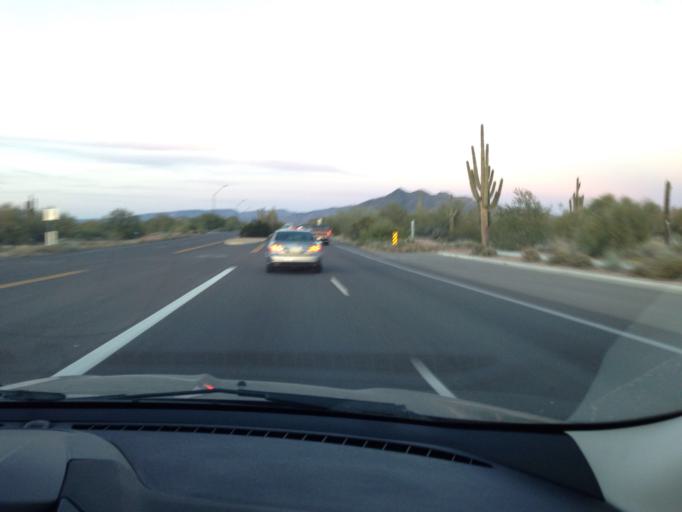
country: US
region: Arizona
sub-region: Maricopa County
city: Cave Creek
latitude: 33.7733
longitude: -111.9798
